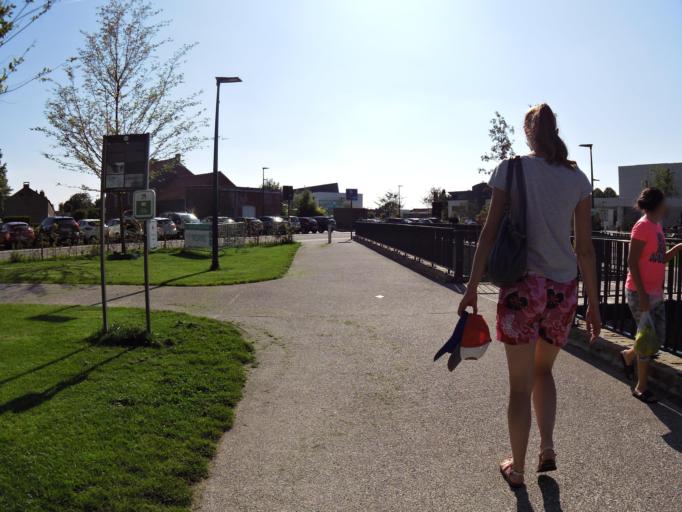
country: BE
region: Flanders
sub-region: Provincie Limburg
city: Tongeren
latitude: 50.7754
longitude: 5.4643
